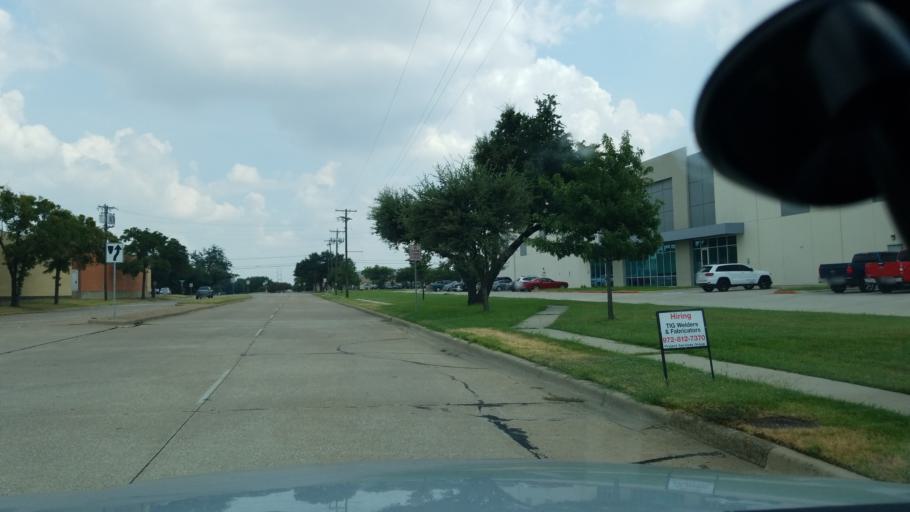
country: US
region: Texas
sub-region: Dallas County
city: Irving
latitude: 32.8353
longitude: -96.8932
